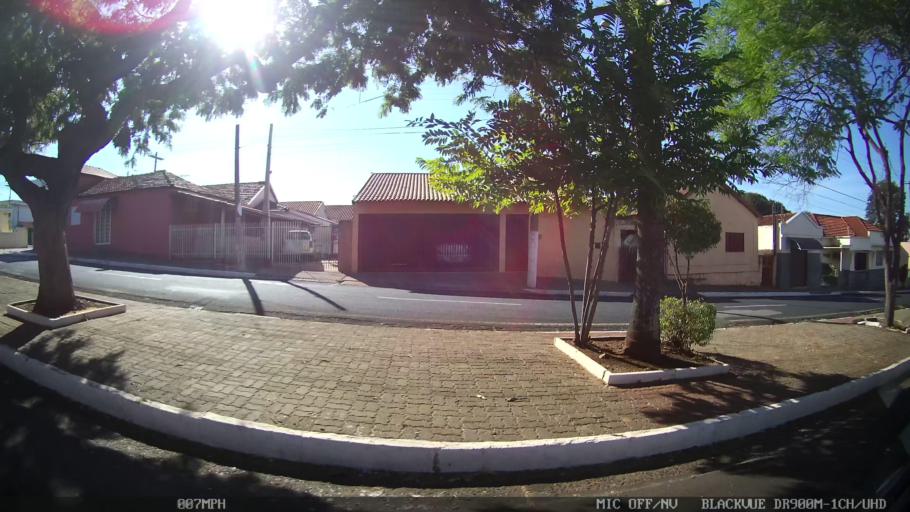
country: BR
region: Sao Paulo
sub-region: Olimpia
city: Olimpia
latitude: -20.7459
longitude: -48.9149
